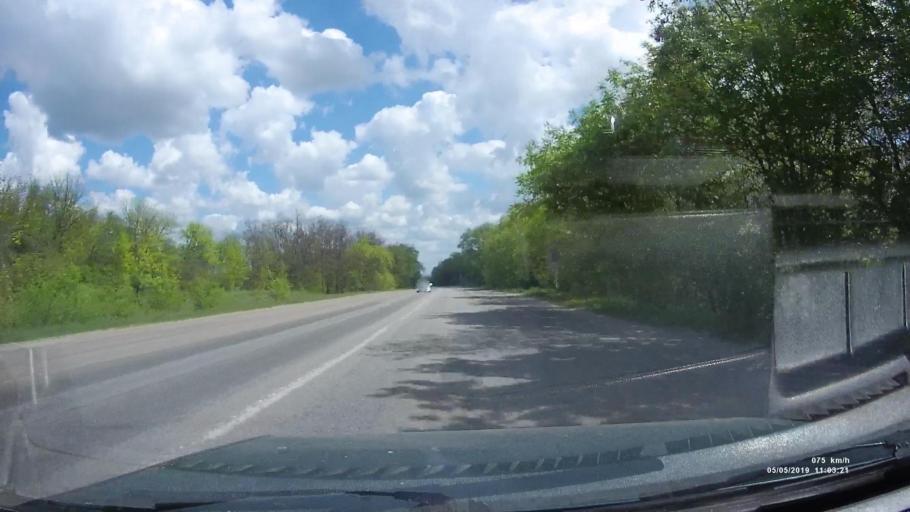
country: RU
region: Rostov
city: Ust'-Donetskiy
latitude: 47.6911
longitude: 40.9195
